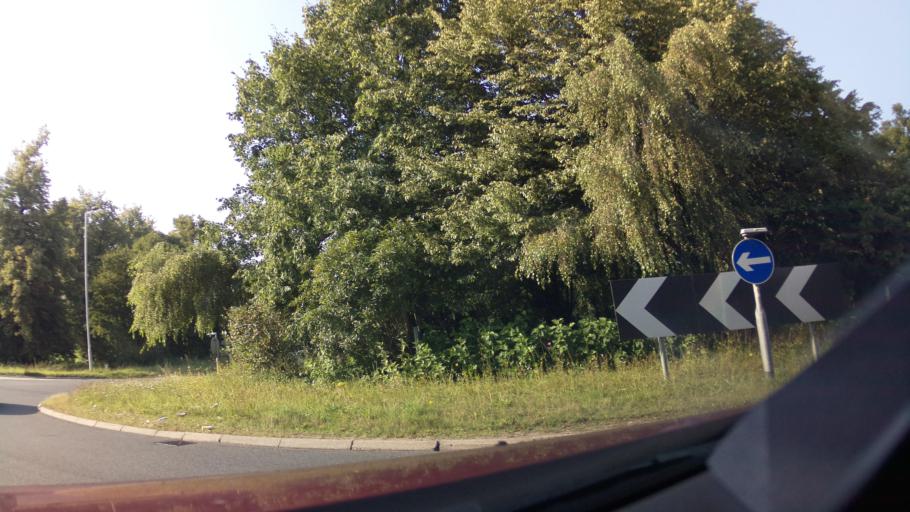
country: GB
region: England
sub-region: Devon
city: Tiverton
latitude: 50.9138
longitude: -3.4925
